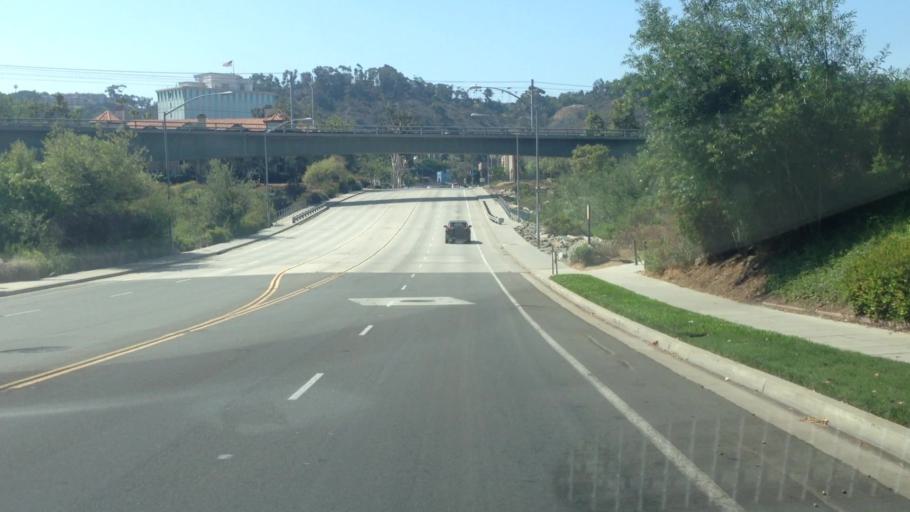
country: US
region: California
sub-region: San Diego County
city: San Diego
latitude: 32.7735
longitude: -117.1451
